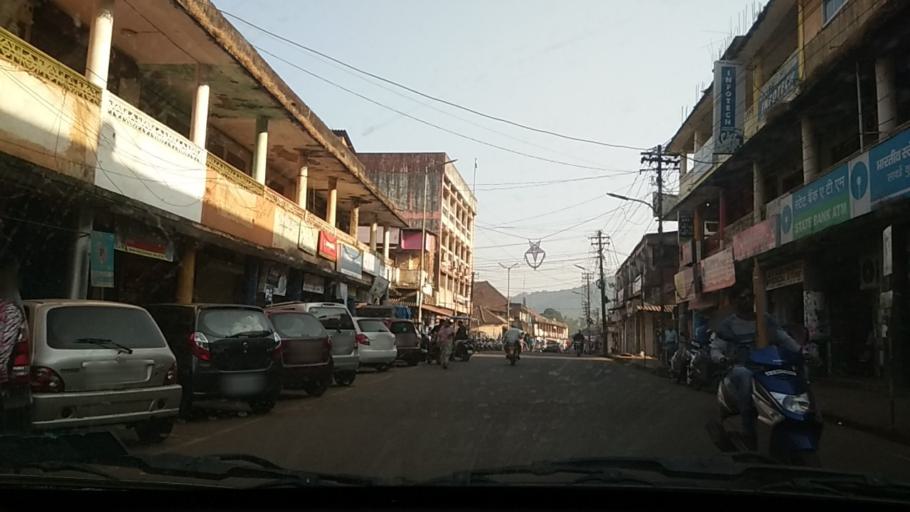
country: IN
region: Goa
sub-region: South Goa
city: Curchorem
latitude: 15.2622
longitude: 74.1075
